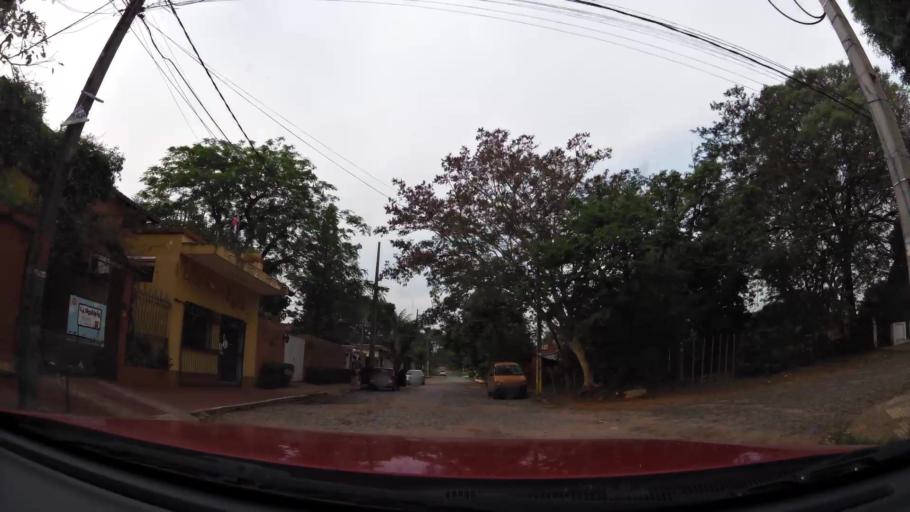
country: PY
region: Asuncion
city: Asuncion
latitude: -25.3116
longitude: -57.6070
